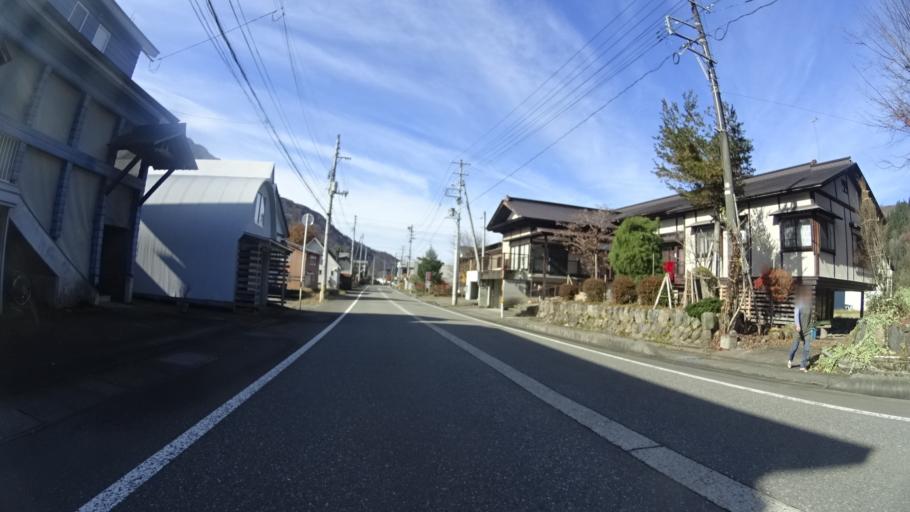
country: JP
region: Niigata
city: Muikamachi
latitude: 37.2140
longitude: 139.0427
